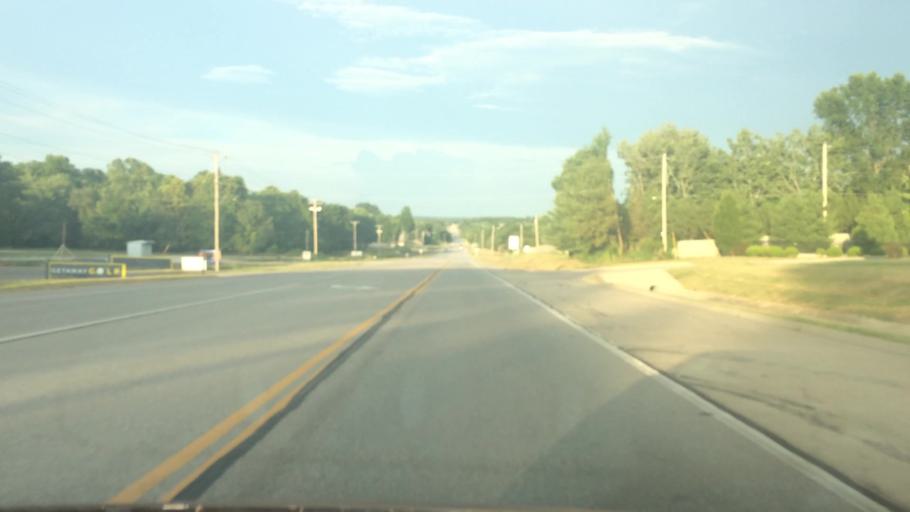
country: US
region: Missouri
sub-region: Greene County
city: Springfield
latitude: 37.1800
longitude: -93.2163
